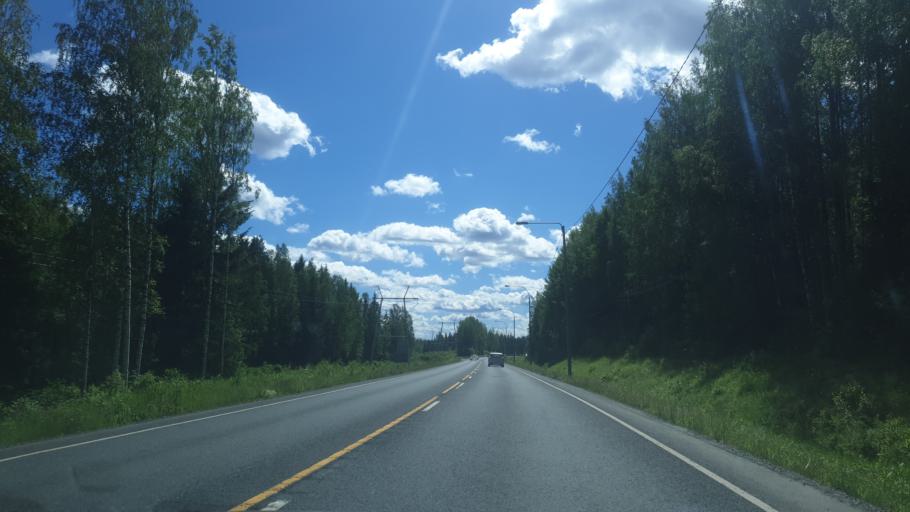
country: FI
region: Northern Savo
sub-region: Varkaus
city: Leppaevirta
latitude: 62.5770
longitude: 27.6046
